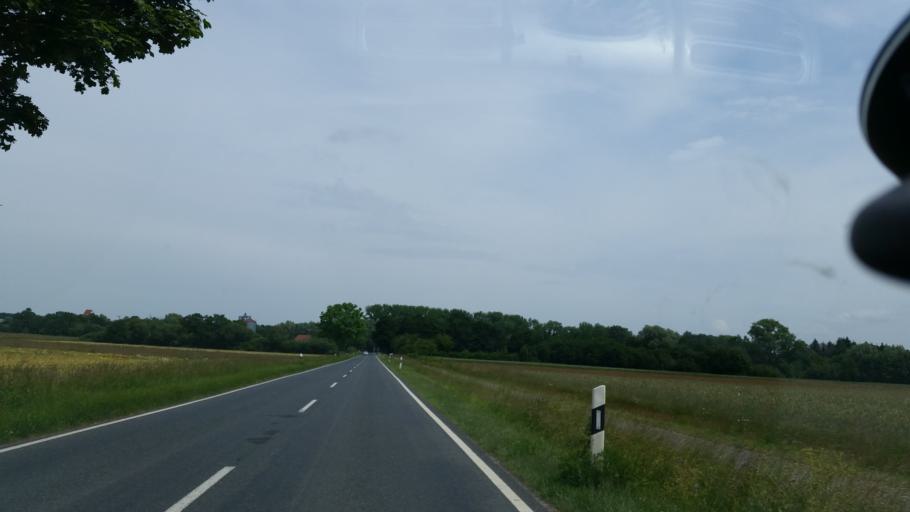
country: DE
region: Lower Saxony
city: Konigslutter am Elm
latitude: 52.3007
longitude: 10.8034
